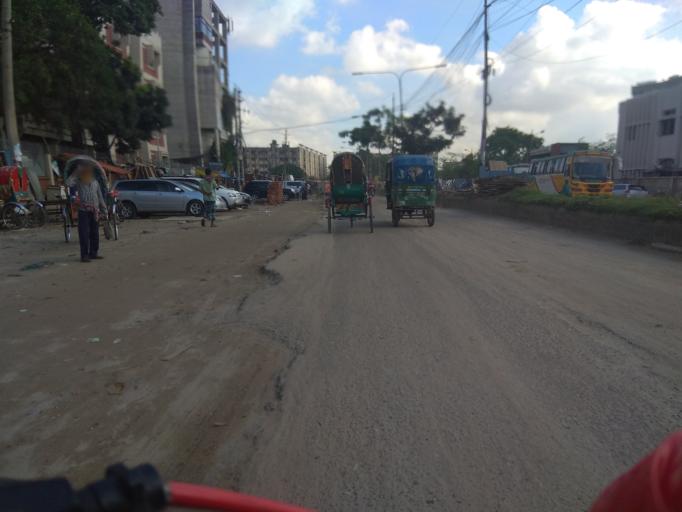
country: BD
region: Dhaka
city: Paltan
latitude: 23.8032
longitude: 90.3877
